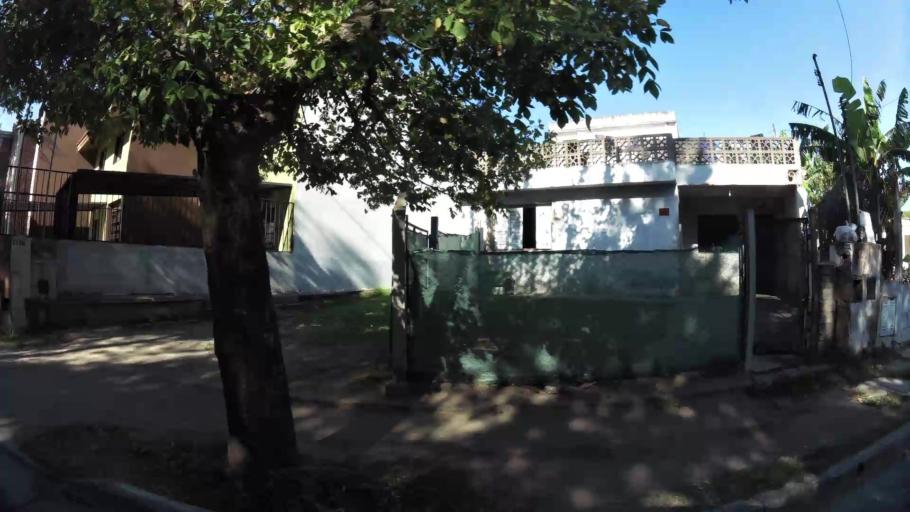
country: AR
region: Cordoba
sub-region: Departamento de Capital
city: Cordoba
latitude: -31.3765
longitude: -64.2490
